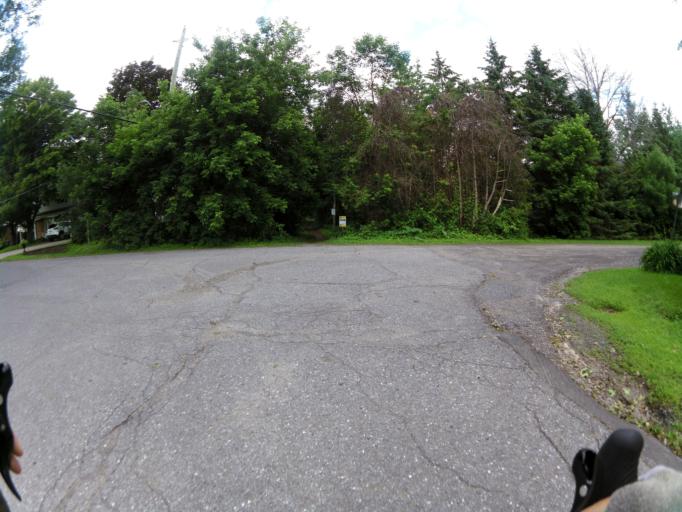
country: CA
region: Ontario
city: Bells Corners
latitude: 45.1846
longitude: -75.8345
